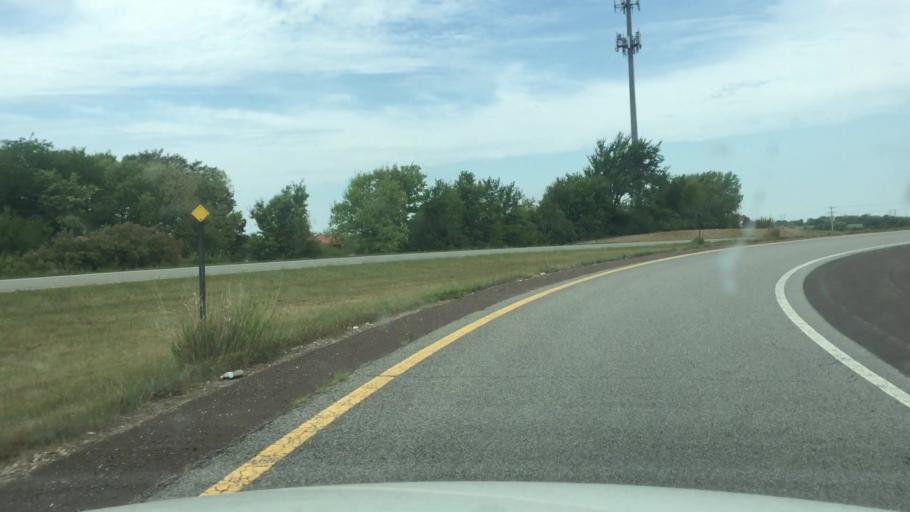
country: US
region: Kansas
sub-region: Wyandotte County
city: Bonner Springs
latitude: 39.0057
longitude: -94.8555
